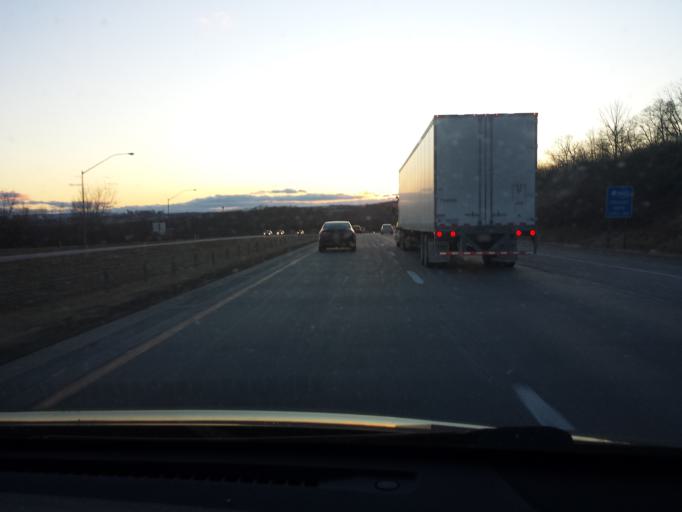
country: US
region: Pennsylvania
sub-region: Centre County
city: Houserville
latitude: 40.8454
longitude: -77.8152
